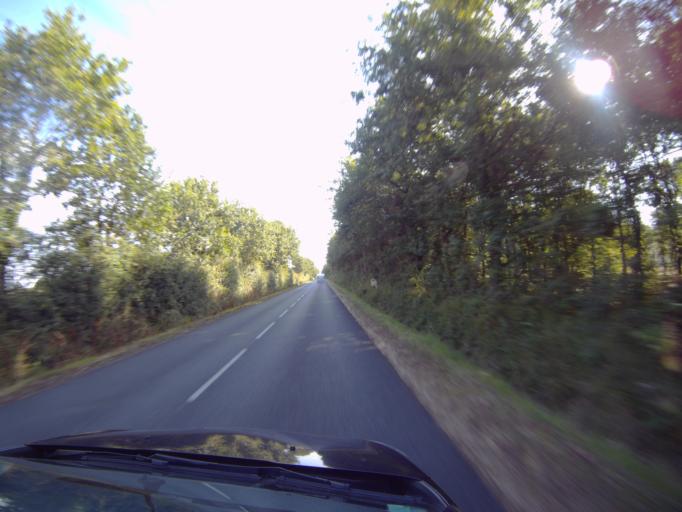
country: FR
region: Pays de la Loire
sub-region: Departement de la Vendee
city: Saint-Hilaire-de-Talmont
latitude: 46.4992
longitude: -1.5794
